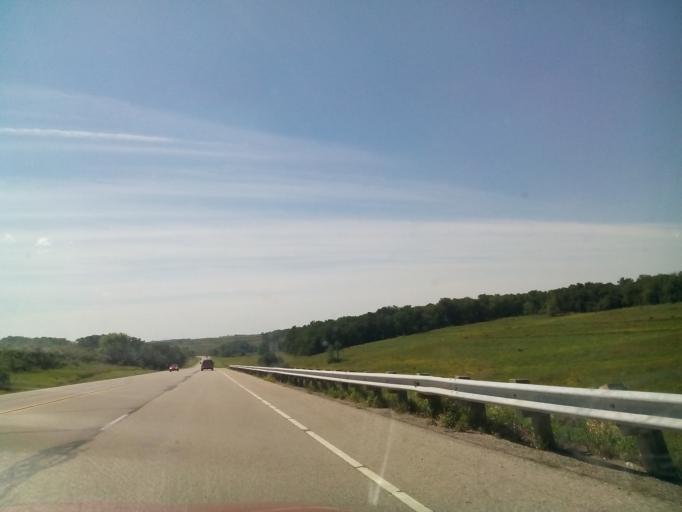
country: US
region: Wisconsin
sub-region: Green County
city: New Glarus
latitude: 42.7830
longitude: -89.6279
